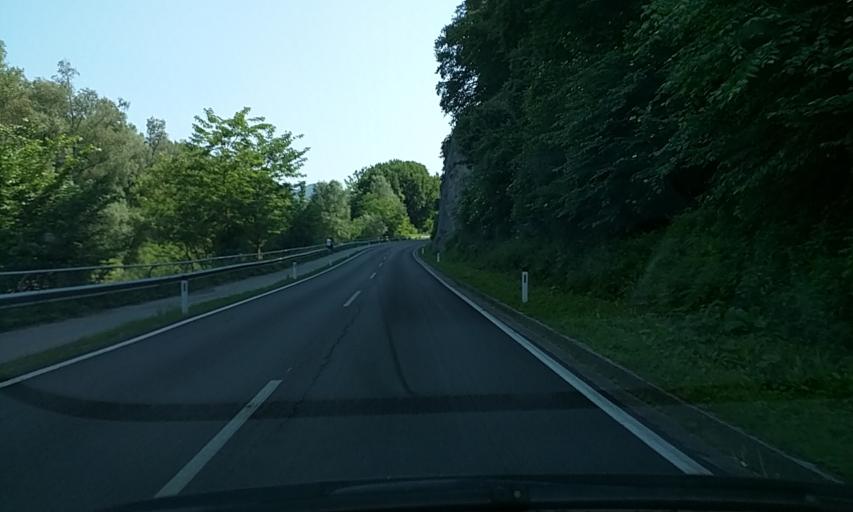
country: AT
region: Lower Austria
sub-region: Politischer Bezirk Krems
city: Aggsbach
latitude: 48.2719
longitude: 15.3884
